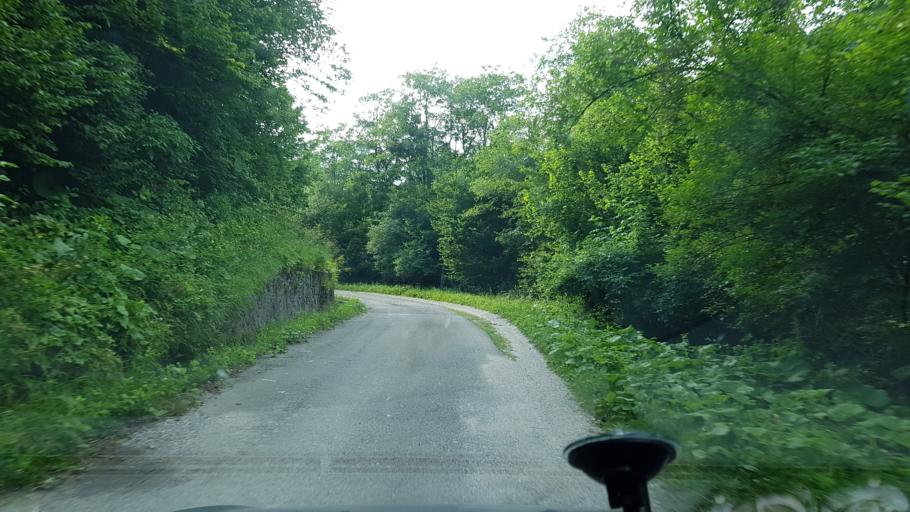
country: IT
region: Friuli Venezia Giulia
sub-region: Provincia di Udine
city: Prato
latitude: 46.3507
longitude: 13.3863
